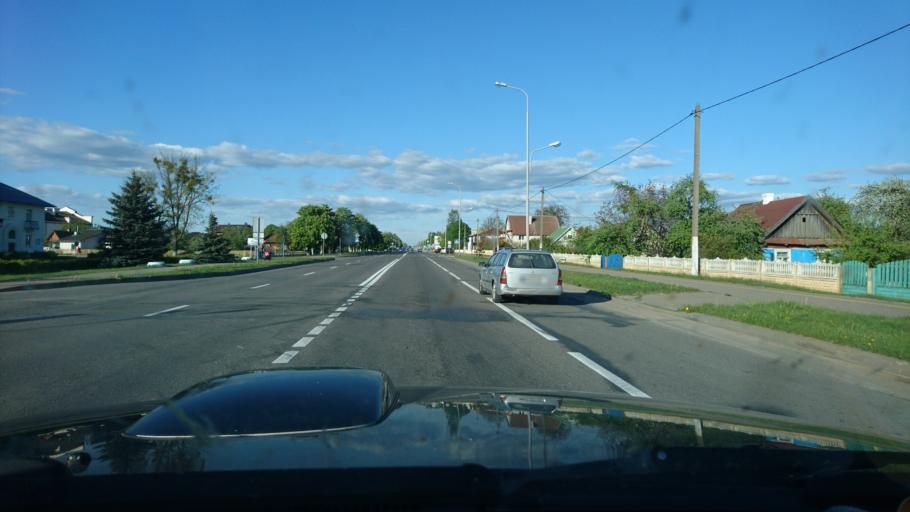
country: BY
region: Brest
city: Ivatsevichy
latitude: 52.7065
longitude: 25.3321
